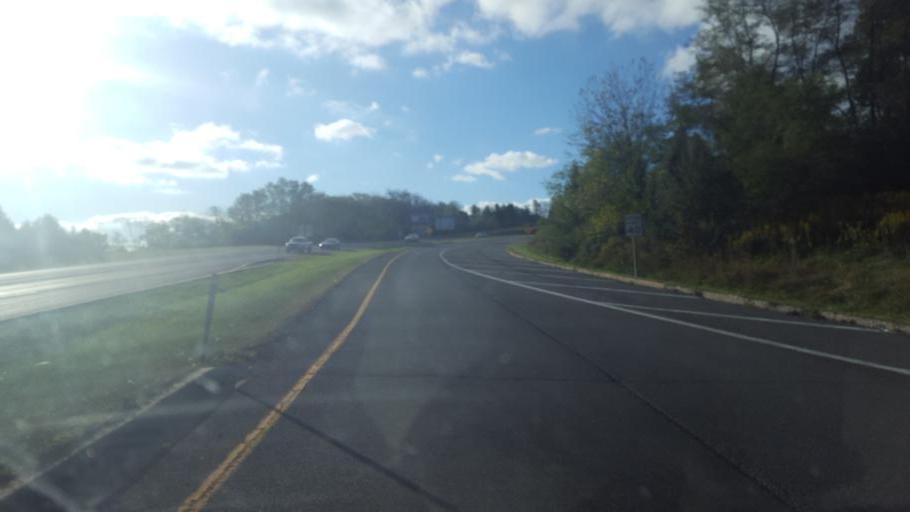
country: US
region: Maryland
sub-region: Allegany County
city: Frostburg
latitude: 39.6499
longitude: -78.9105
